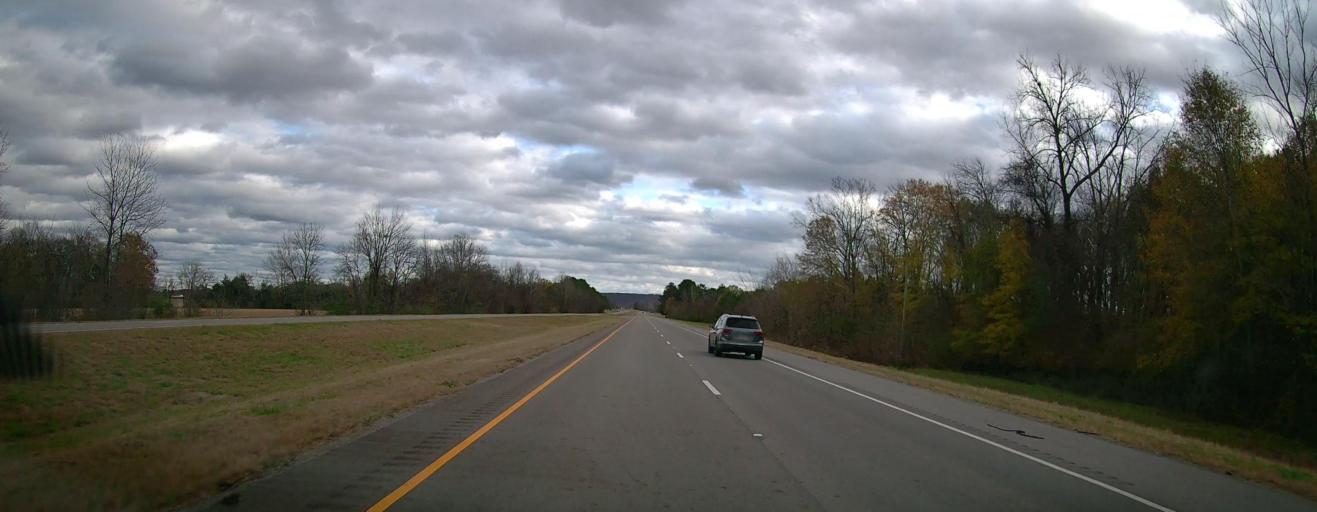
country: US
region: Alabama
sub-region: Morgan County
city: Danville
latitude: 34.3504
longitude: -87.0436
